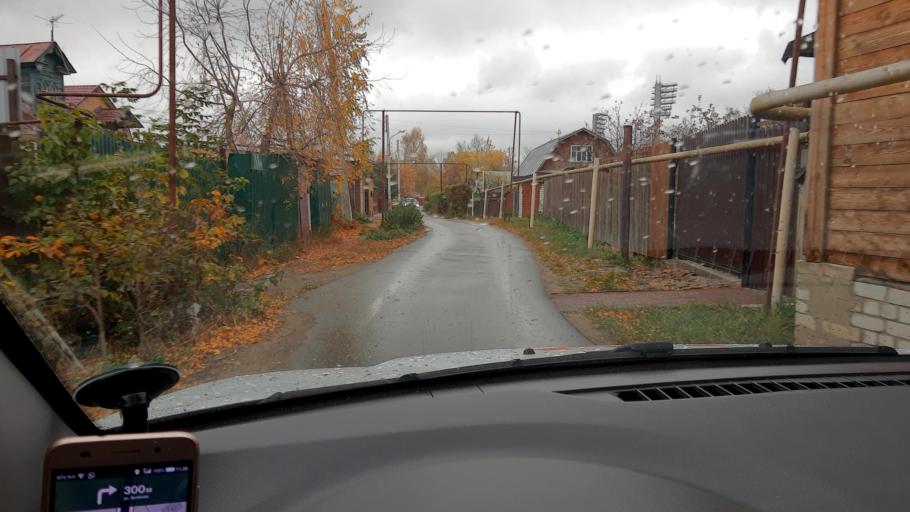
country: RU
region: Nizjnij Novgorod
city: Nizhniy Novgorod
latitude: 56.3057
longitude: 43.9267
